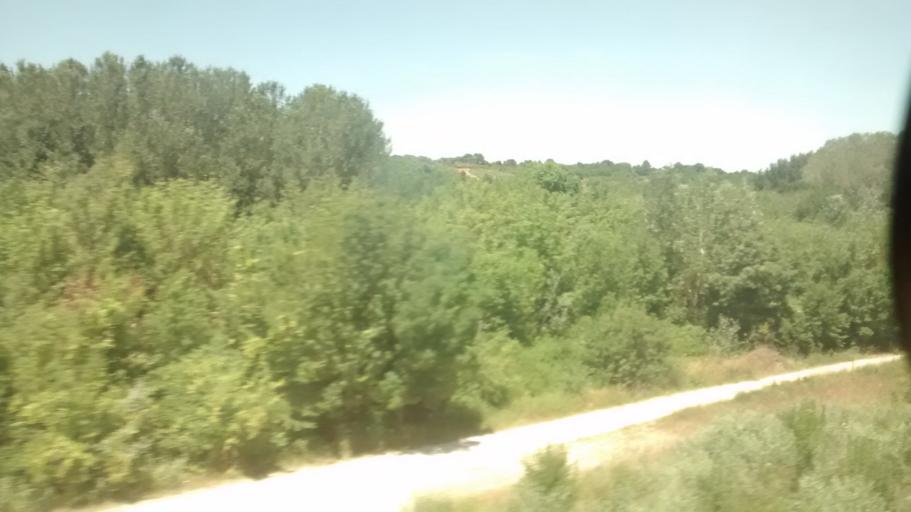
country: FR
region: Languedoc-Roussillon
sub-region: Departement du Gard
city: Montfrin
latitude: 43.8709
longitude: 4.6074
